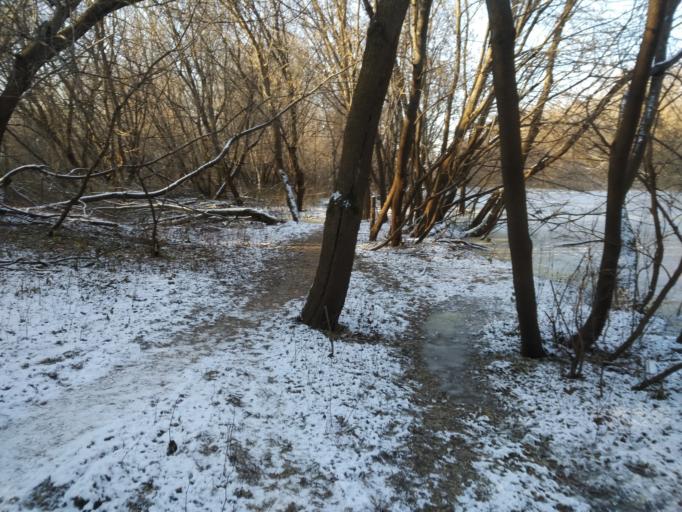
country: RU
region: Kirov
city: Vyatskiye Polyany
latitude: 56.2381
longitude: 51.0793
